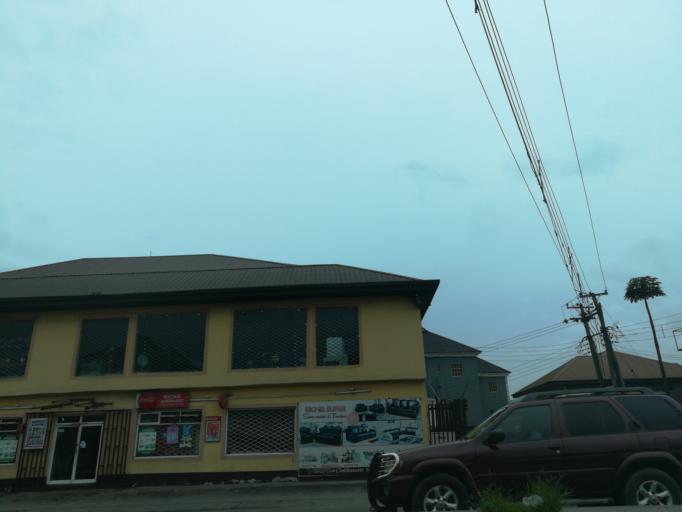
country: NG
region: Rivers
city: Port Harcourt
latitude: 4.8345
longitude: 7.0257
